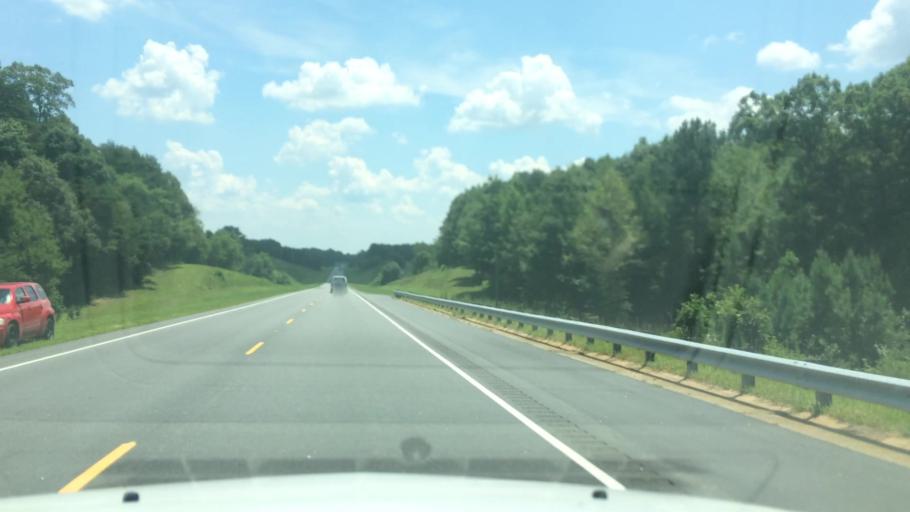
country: US
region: North Carolina
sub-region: Alexander County
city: Stony Point
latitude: 35.8835
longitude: -81.0752
